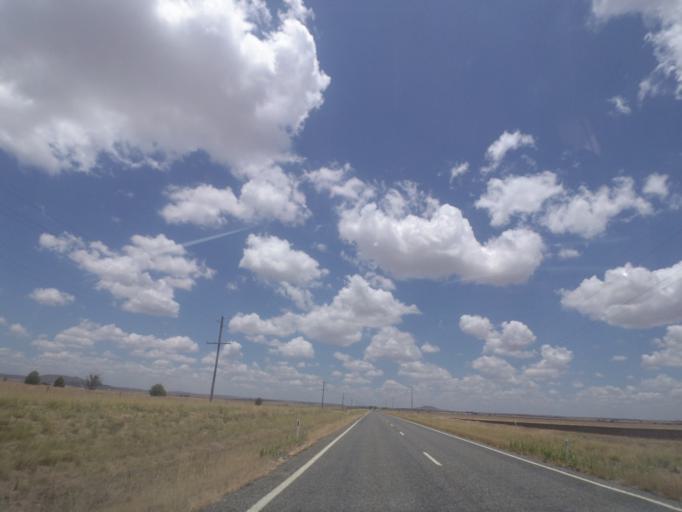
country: AU
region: Queensland
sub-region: Toowoomba
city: Top Camp
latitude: -27.9020
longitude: 151.9766
